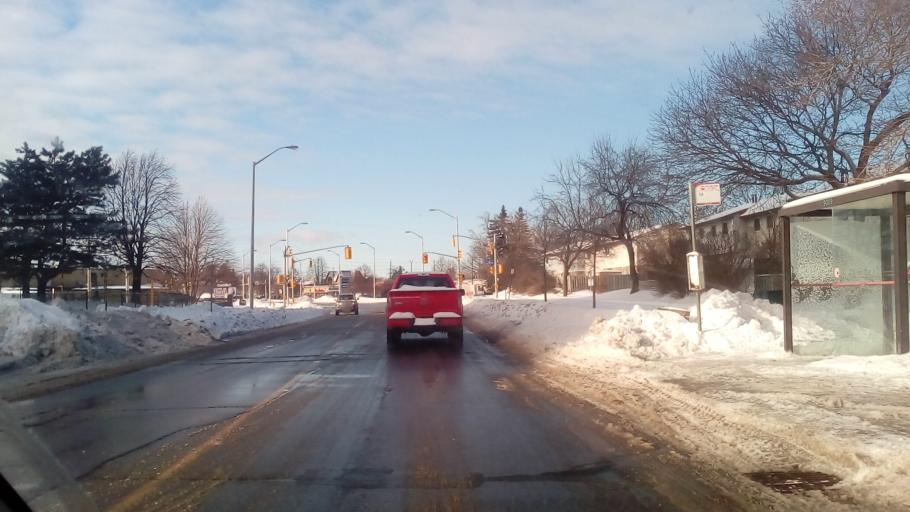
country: CA
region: Ontario
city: Ottawa
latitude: 45.4287
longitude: -75.6358
